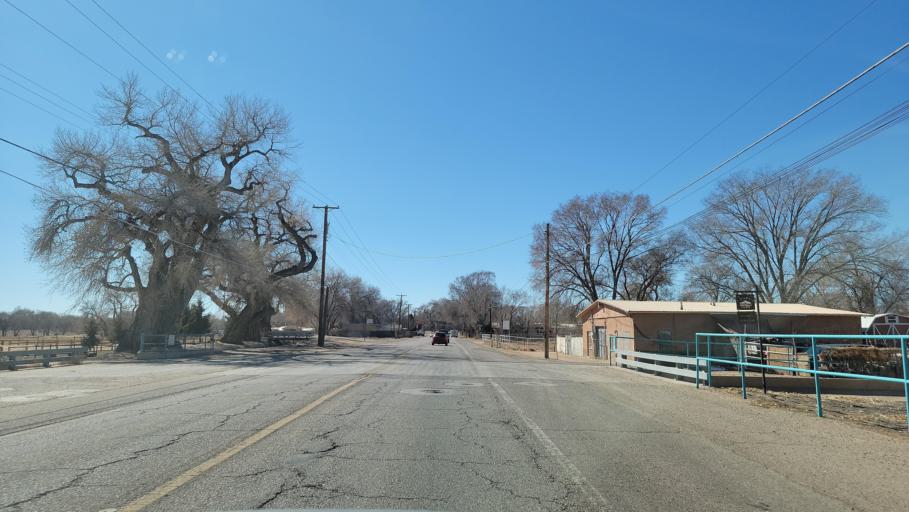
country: US
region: New Mexico
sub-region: Bernalillo County
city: South Valley
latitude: 35.0042
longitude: -106.6902
